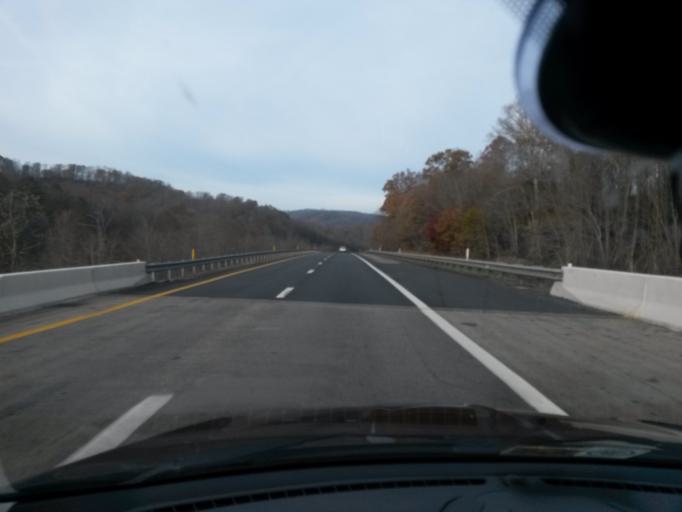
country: US
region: West Virginia
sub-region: Raleigh County
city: Prosperity
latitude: 37.8464
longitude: -81.2390
